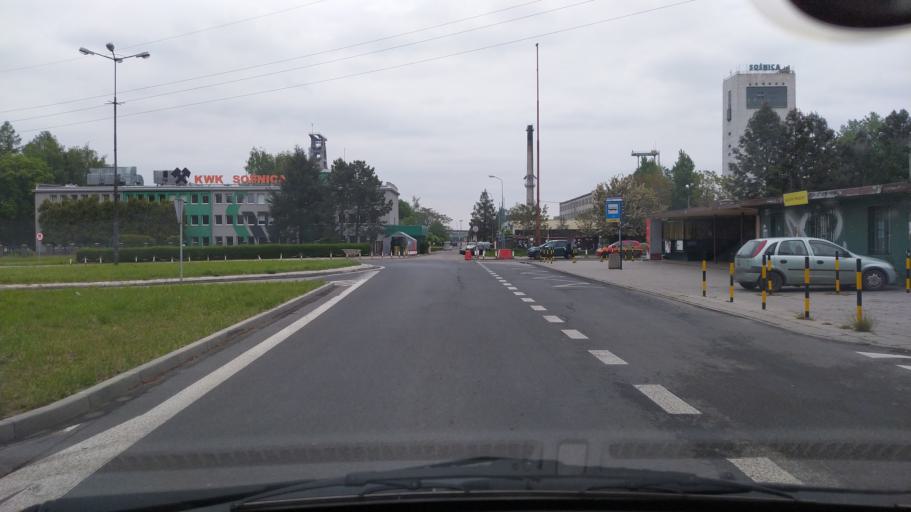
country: PL
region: Silesian Voivodeship
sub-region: Gliwice
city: Gliwice
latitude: 50.2746
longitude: 18.7067
